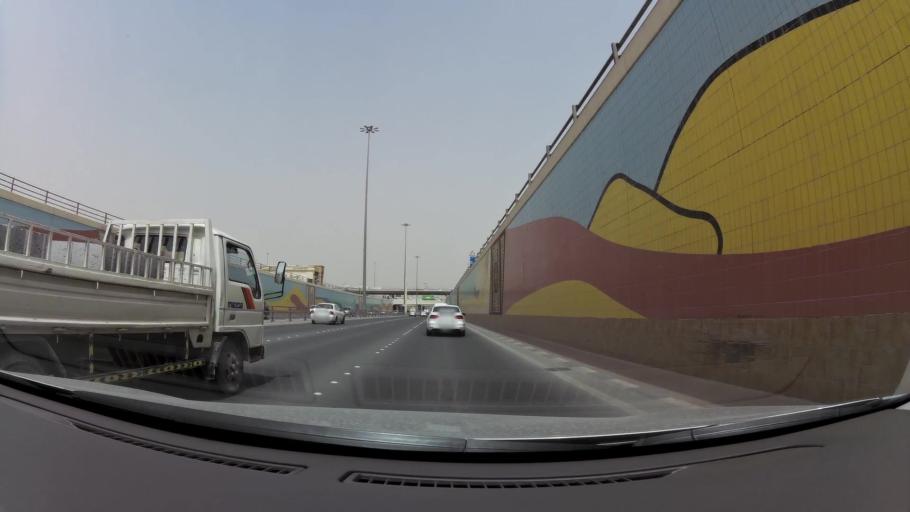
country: QA
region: Baladiyat ad Dawhah
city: Doha
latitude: 25.2619
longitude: 51.4986
